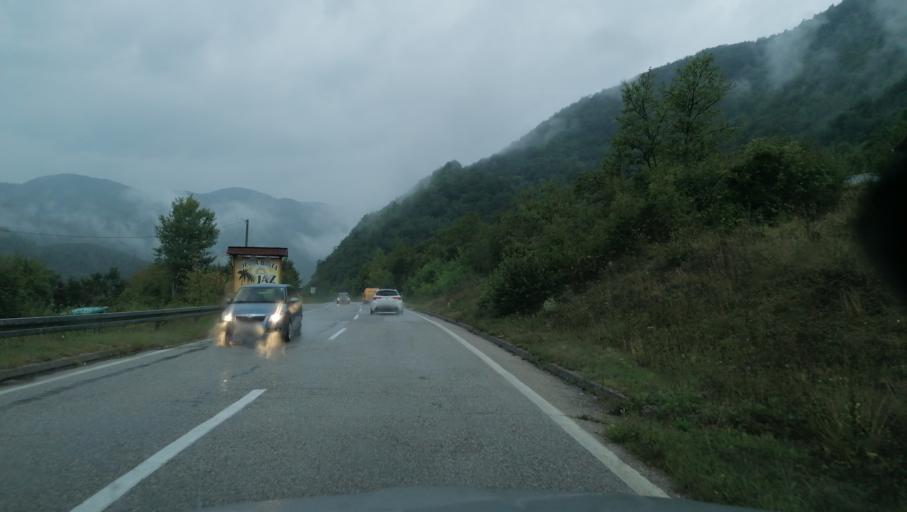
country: BA
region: Republika Srpska
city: Visegrad
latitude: 43.7156
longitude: 19.1681
